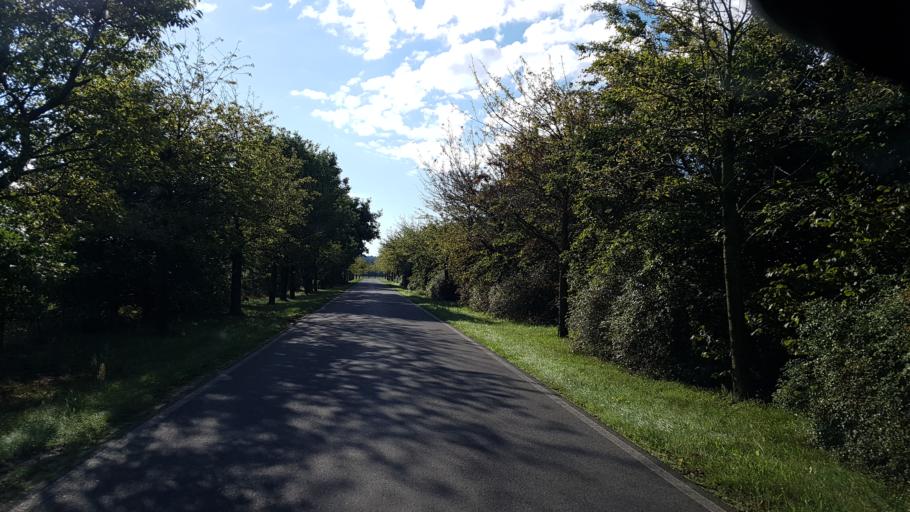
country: DE
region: Saxony
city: Gross Duben
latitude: 51.6281
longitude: 14.5302
